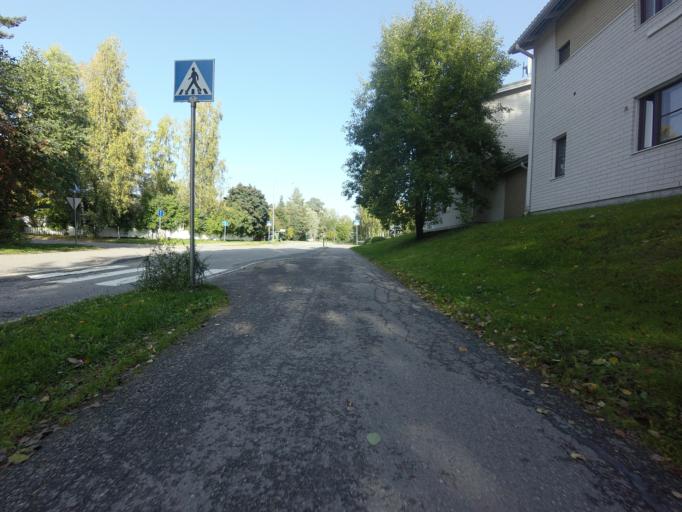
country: FI
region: Uusimaa
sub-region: Helsinki
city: Espoo
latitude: 60.1793
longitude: 24.6647
